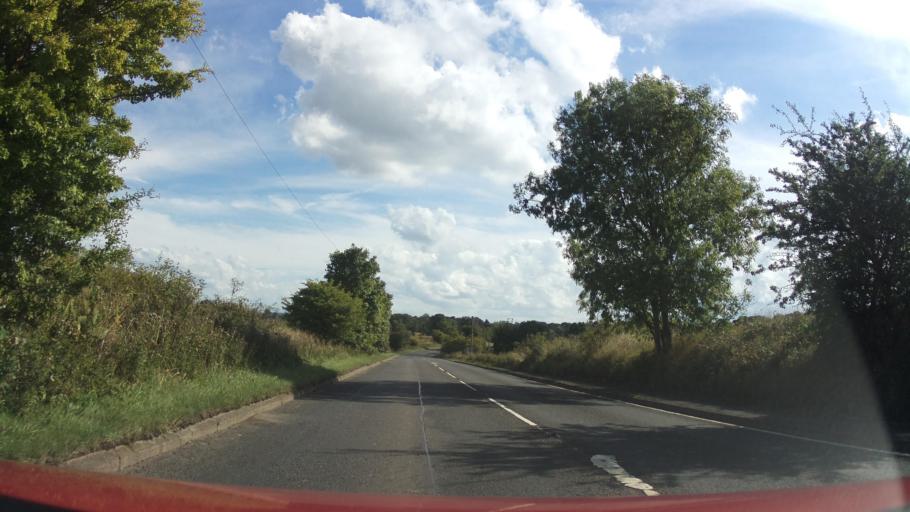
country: GB
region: Scotland
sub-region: Stirling
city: Cowie
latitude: 56.0520
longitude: -3.8598
